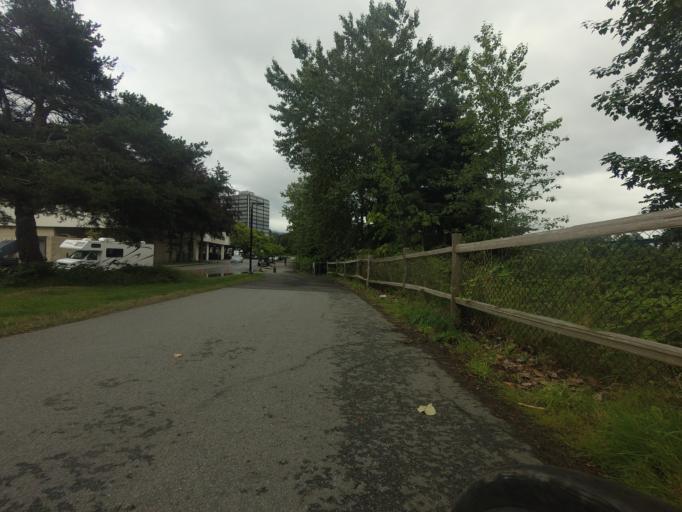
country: CA
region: British Columbia
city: West End
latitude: 49.3238
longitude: -123.1365
